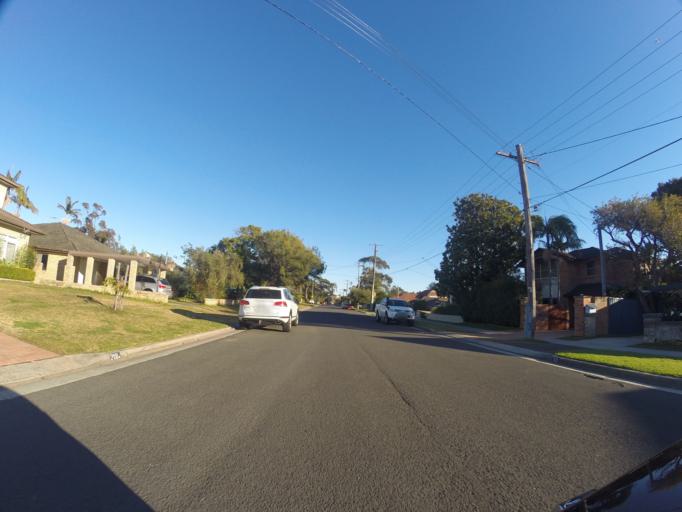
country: AU
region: New South Wales
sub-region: Sutherland Shire
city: Gymea Bay
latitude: -34.0537
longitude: 151.0904
